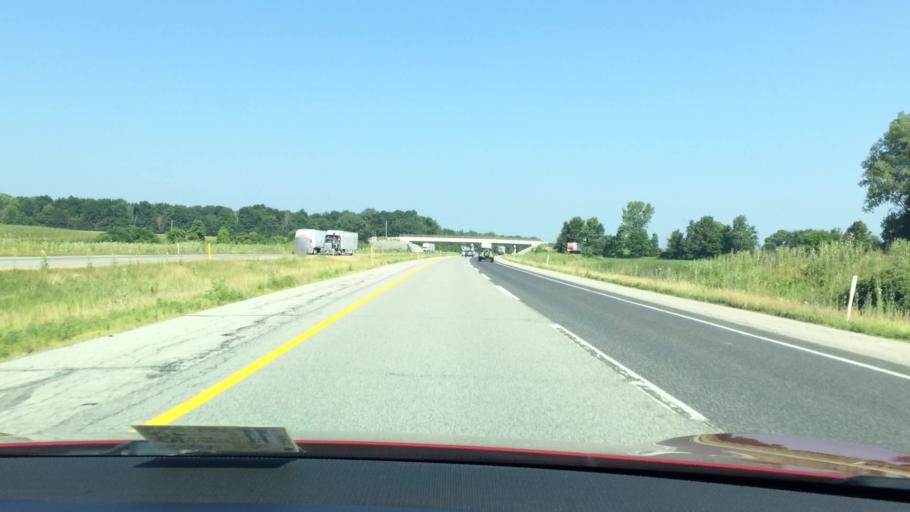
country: US
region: Indiana
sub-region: Steuben County
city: Fremont
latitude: 41.6926
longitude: -84.9030
